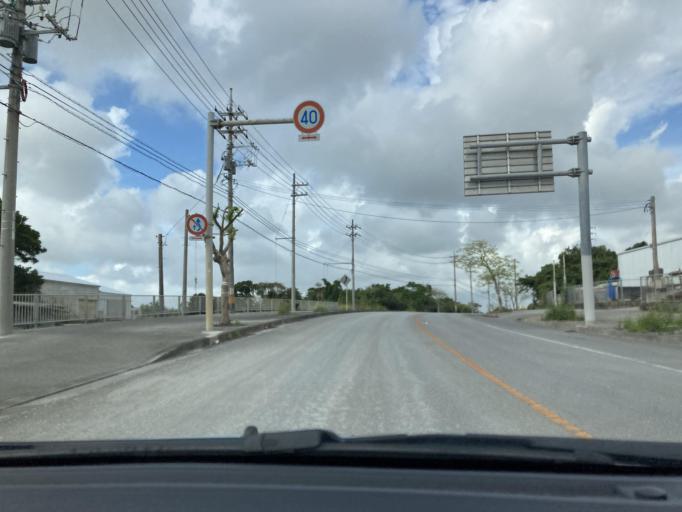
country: JP
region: Okinawa
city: Itoman
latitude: 26.1205
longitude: 127.6921
